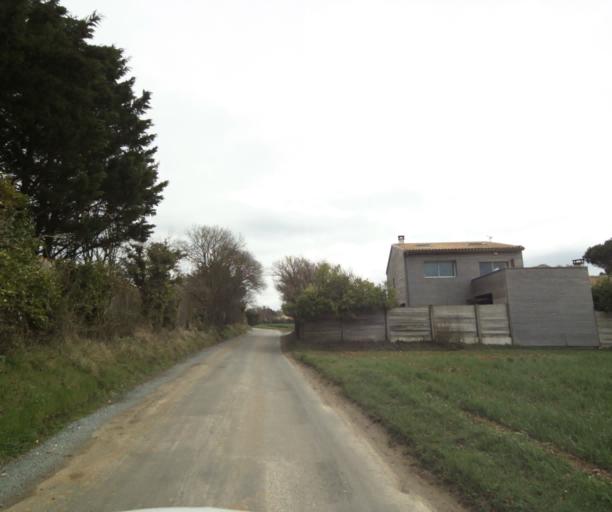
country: FR
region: Poitou-Charentes
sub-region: Departement de la Charente-Maritime
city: Lagord
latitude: 46.1897
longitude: -1.1701
